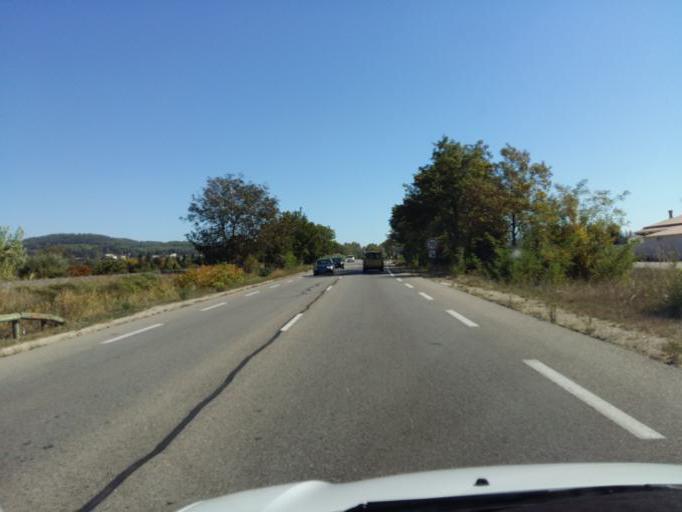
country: FR
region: Provence-Alpes-Cote d'Azur
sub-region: Departement du Vaucluse
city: Cadenet
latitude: 43.7309
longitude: 5.3634
